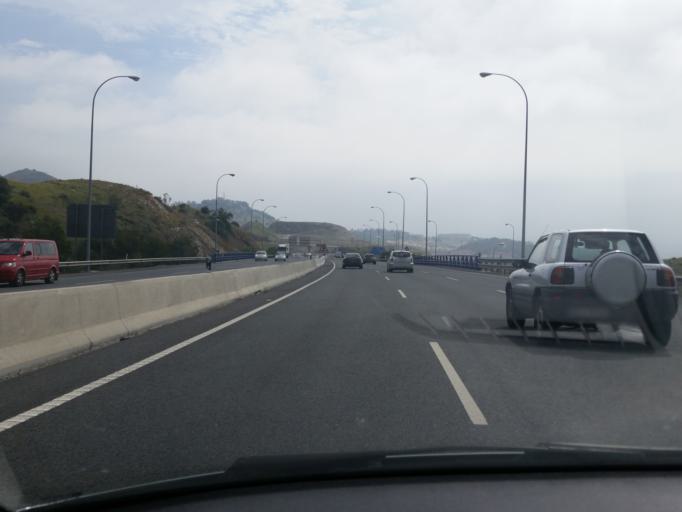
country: ES
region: Andalusia
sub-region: Provincia de Malaga
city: Malaga
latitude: 36.7435
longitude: -4.4060
